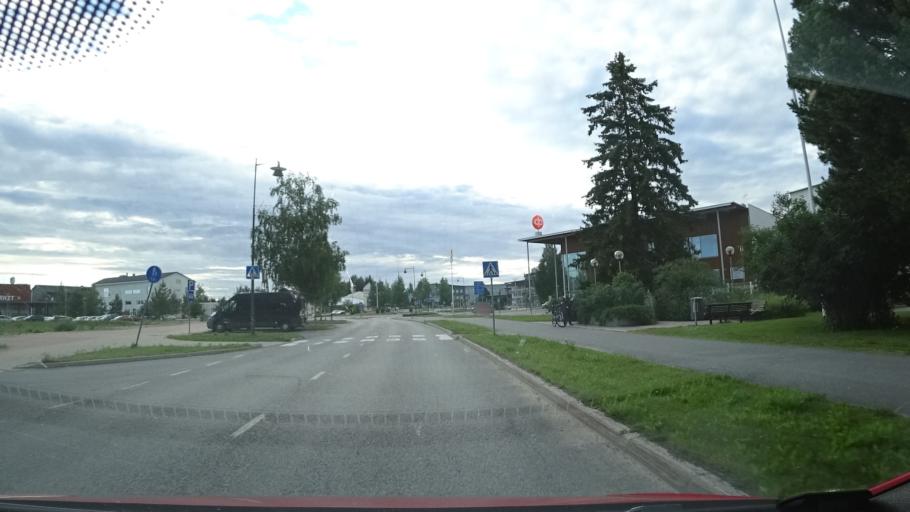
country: FI
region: Northern Ostrobothnia
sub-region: Oulu
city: Liminka
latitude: 64.8093
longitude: 25.4177
